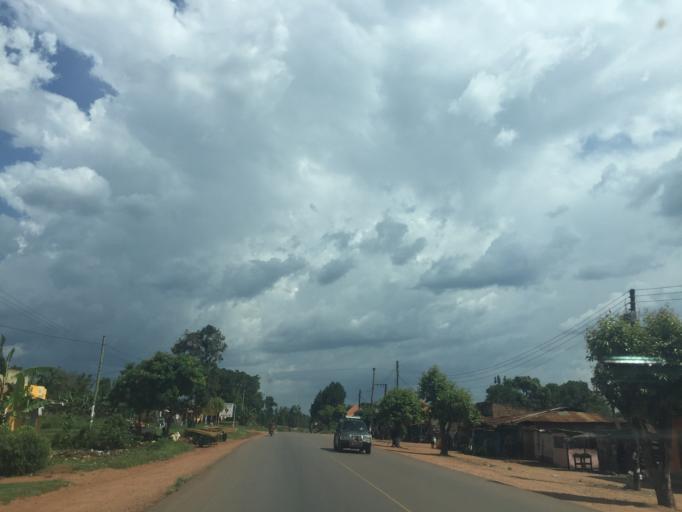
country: UG
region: Central Region
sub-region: Luwero District
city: Wobulenzi
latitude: 0.7334
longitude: 32.5253
